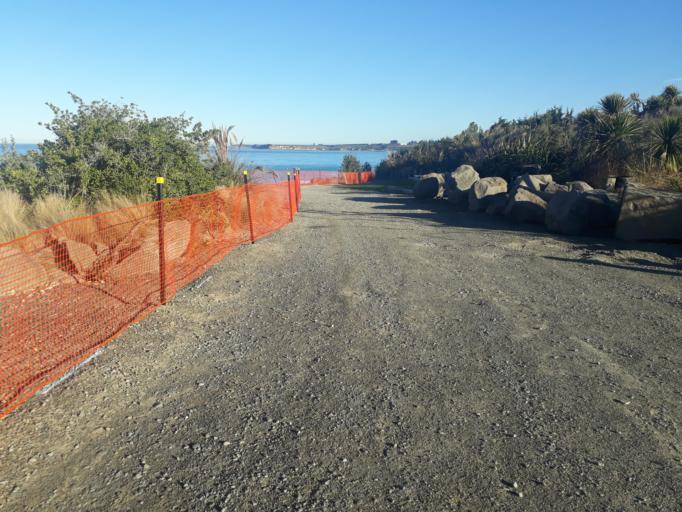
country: NZ
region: Canterbury
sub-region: Timaru District
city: Timaru
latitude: -44.4150
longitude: 171.2642
